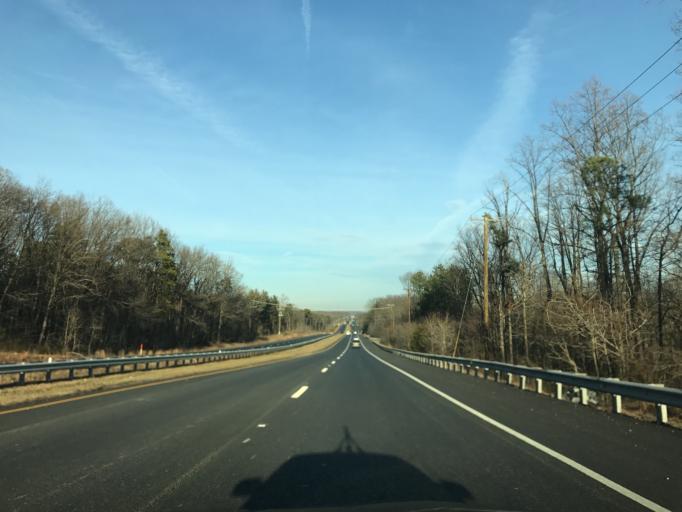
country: US
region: Maryland
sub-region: Cecil County
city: Charlestown
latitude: 39.5888
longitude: -76.0004
